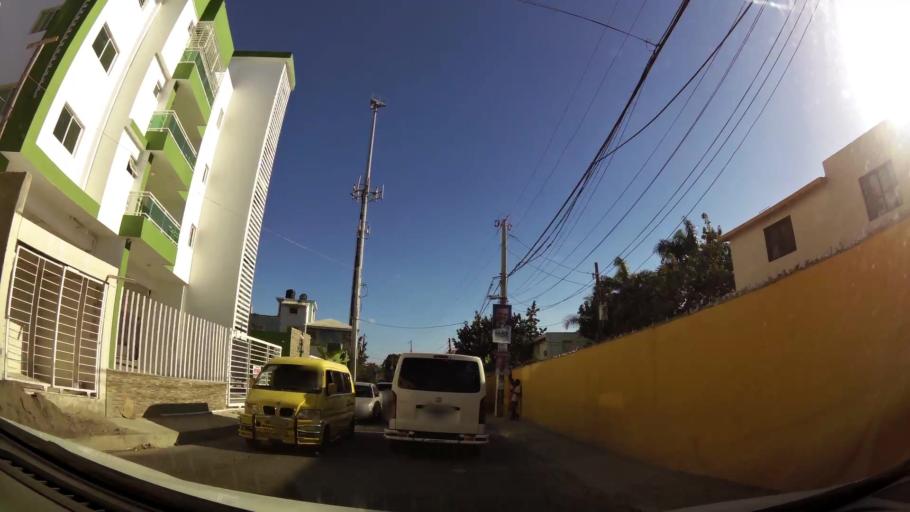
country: DO
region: Santo Domingo
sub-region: Santo Domingo
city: Santo Domingo Este
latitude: 18.4939
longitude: -69.8067
